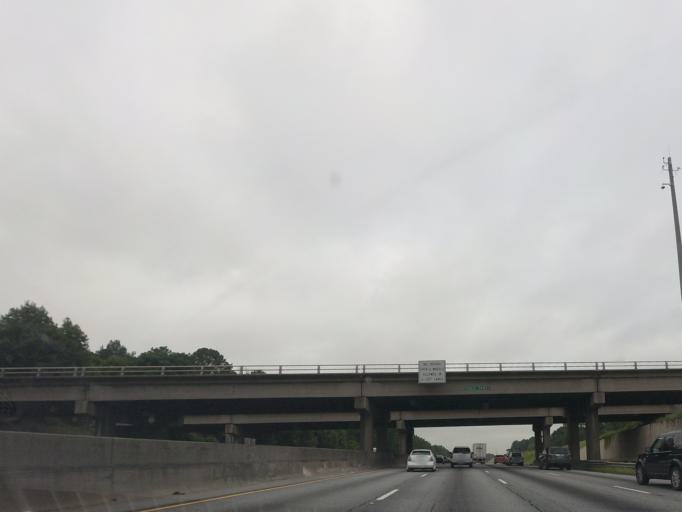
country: US
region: Georgia
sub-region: Clayton County
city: Forest Park
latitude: 33.6172
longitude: -84.3982
